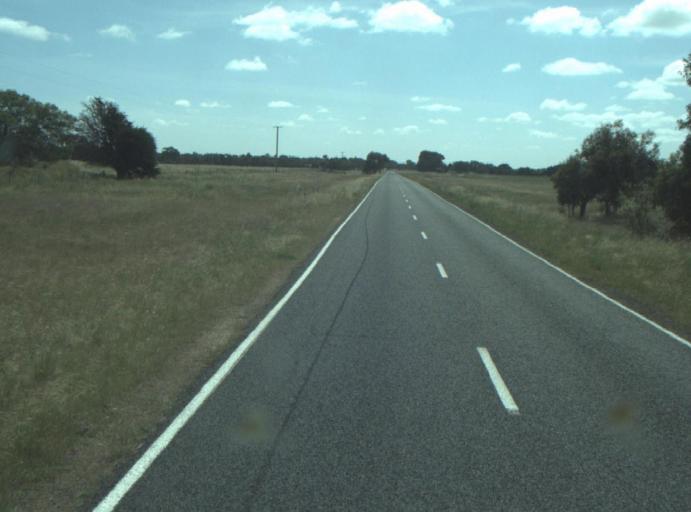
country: AU
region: Victoria
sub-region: Wyndham
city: Little River
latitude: -37.9946
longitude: 144.4825
